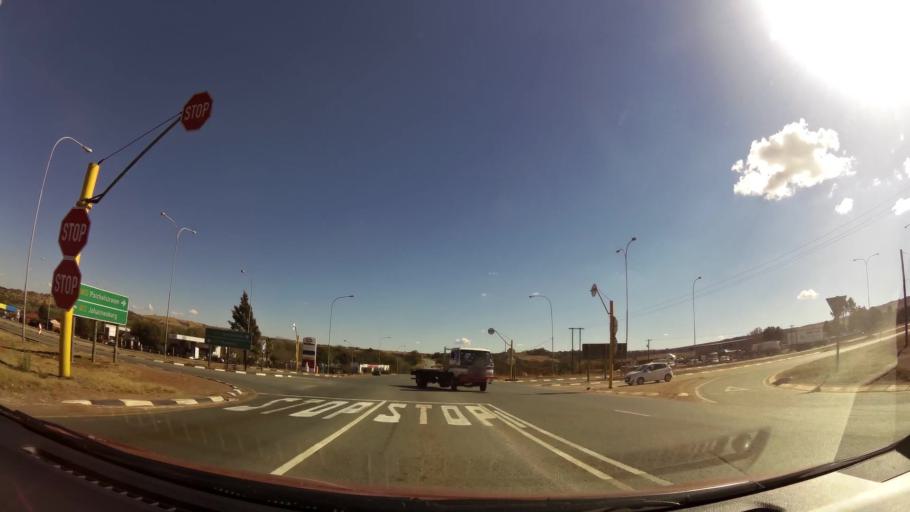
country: ZA
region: North-West
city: Fochville
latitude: -26.4413
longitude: 27.4839
